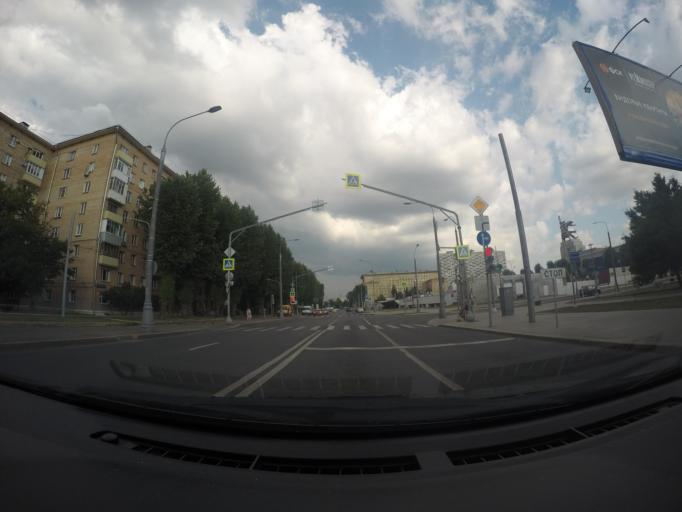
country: RU
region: Moscow
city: Leonovo
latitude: 55.8304
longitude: 37.6457
